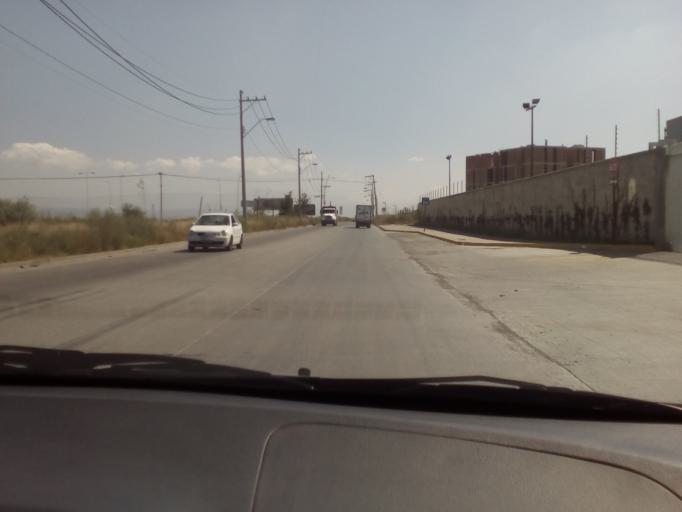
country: MX
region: Guanajuato
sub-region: Leon
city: Fraccionamiento Paseo de las Torres
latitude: 21.1715
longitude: -101.7546
